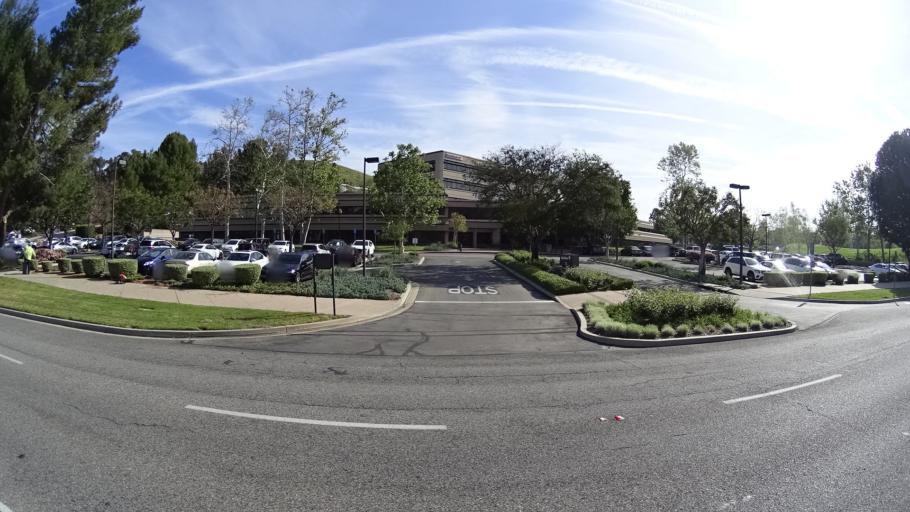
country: US
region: California
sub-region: Ventura County
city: Thousand Oaks
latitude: 34.1822
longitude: -118.8830
